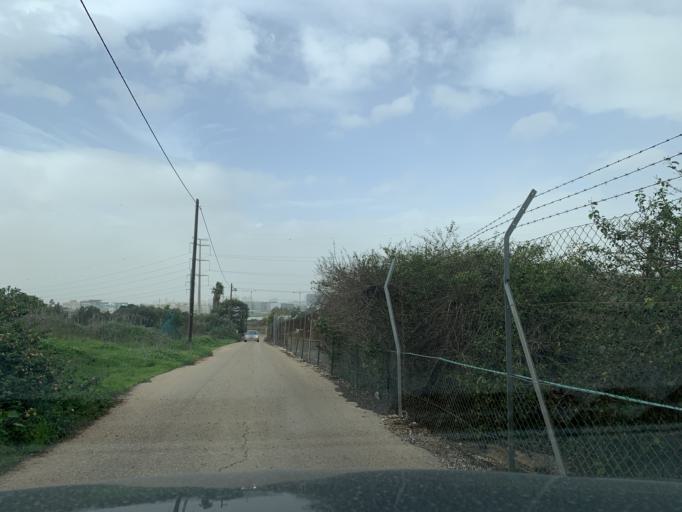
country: IL
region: Central District
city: Jaljulya
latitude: 32.1629
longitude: 34.9440
